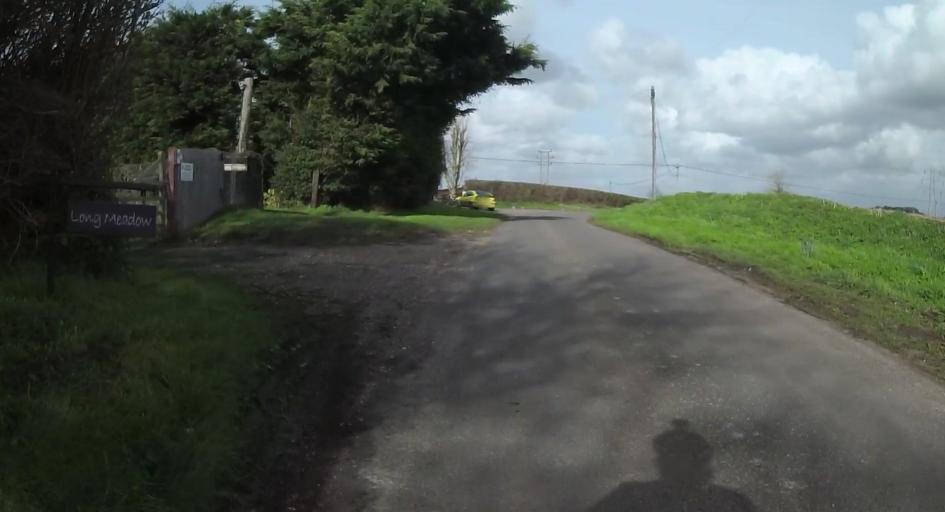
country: GB
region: England
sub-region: Hampshire
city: Kingsclere
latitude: 51.3382
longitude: -1.2438
